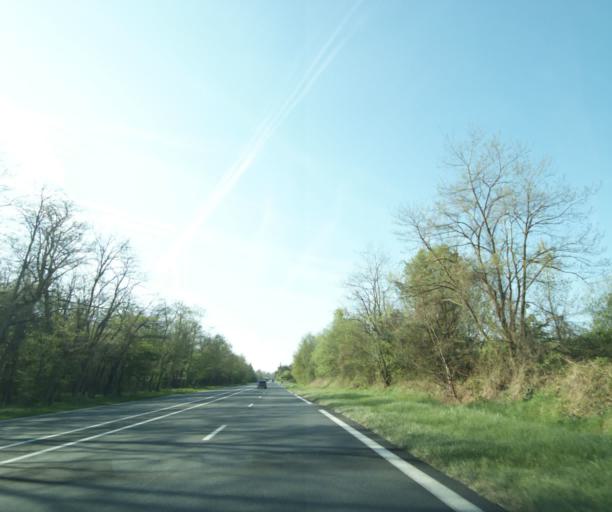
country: FR
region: Ile-de-France
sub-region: Departement de Seine-et-Marne
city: Grez-sur-Loing
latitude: 48.2990
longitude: 2.6791
